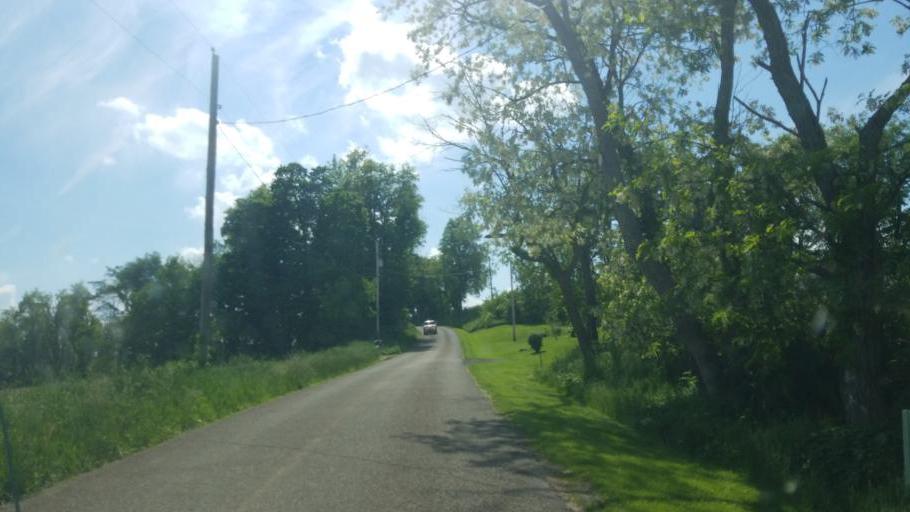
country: US
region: Ohio
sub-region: Sandusky County
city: Bellville
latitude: 40.6625
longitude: -82.5292
